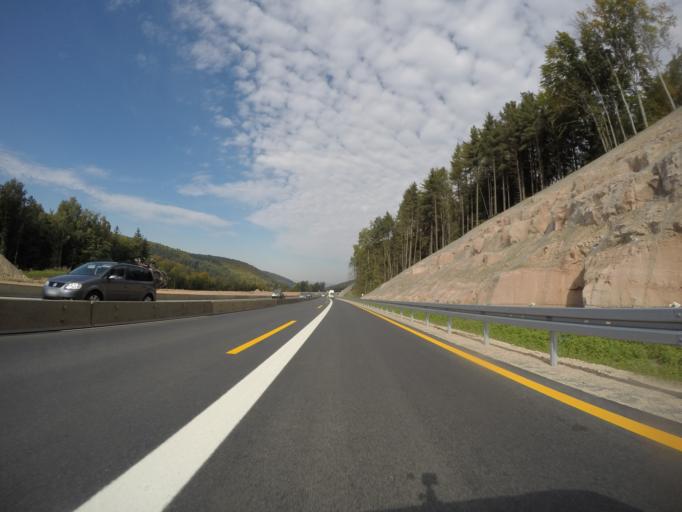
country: DE
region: Bavaria
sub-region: Regierungsbezirk Unterfranken
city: Waldaschaff
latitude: 49.9516
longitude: 9.3295
